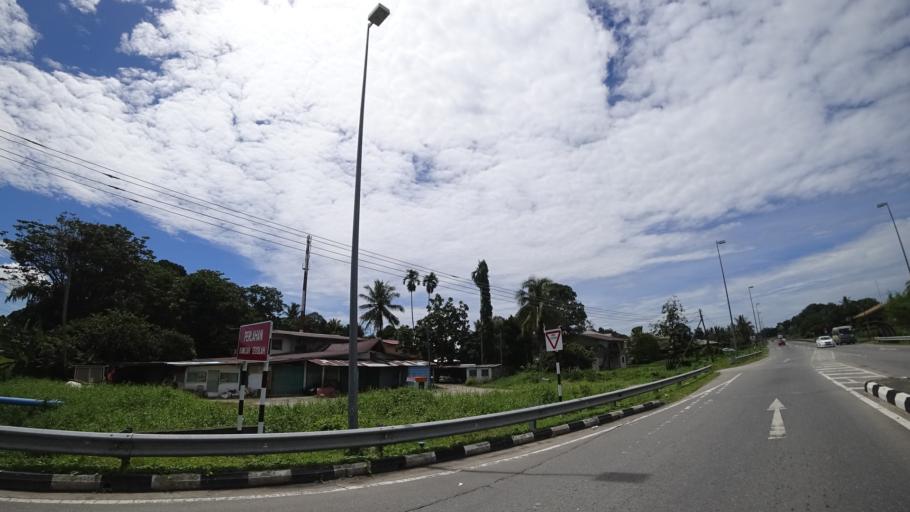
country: BN
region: Brunei and Muara
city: Bandar Seri Begawan
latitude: 4.8274
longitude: 114.8441
